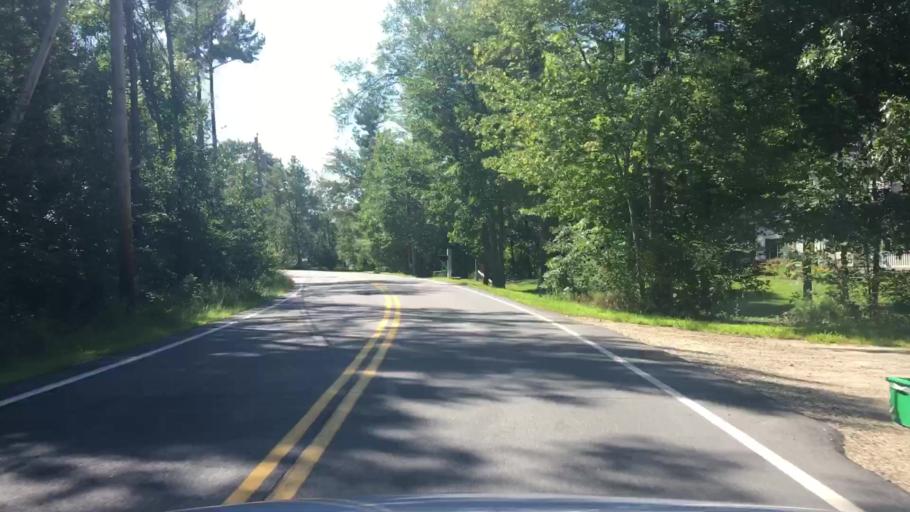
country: US
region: New Hampshire
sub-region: Strafford County
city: Dover
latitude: 43.1857
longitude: -70.8483
